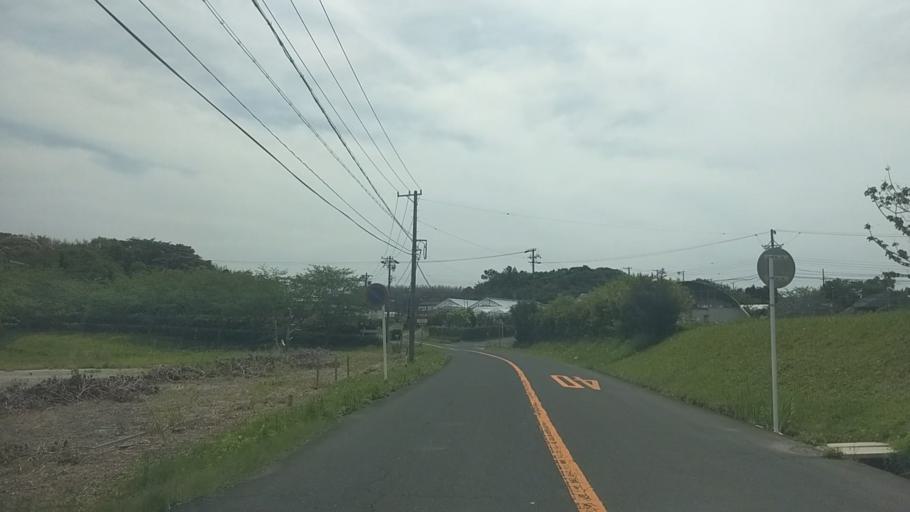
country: JP
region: Shizuoka
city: Kosai-shi
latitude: 34.7539
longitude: 137.5183
